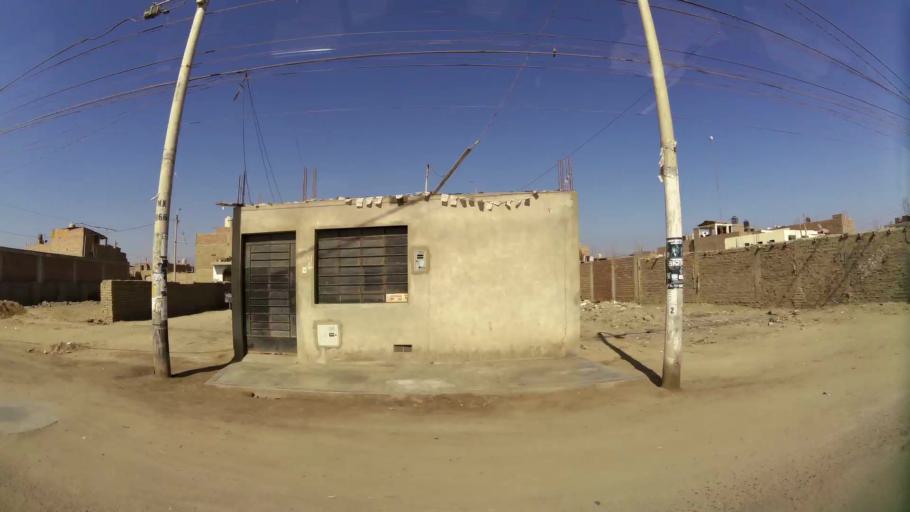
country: PE
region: Ica
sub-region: Provincia de Chincha
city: Chincha Alta
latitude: -13.4136
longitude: -76.1273
